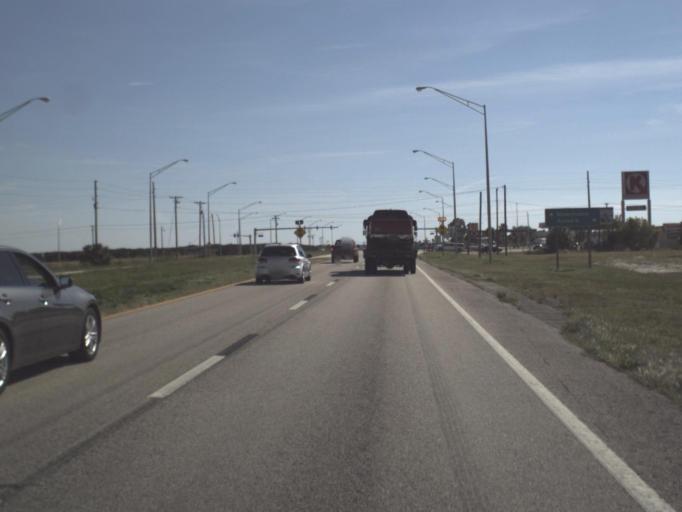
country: US
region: Florida
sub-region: Highlands County
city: Placid Lakes
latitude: 27.2110
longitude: -81.3288
